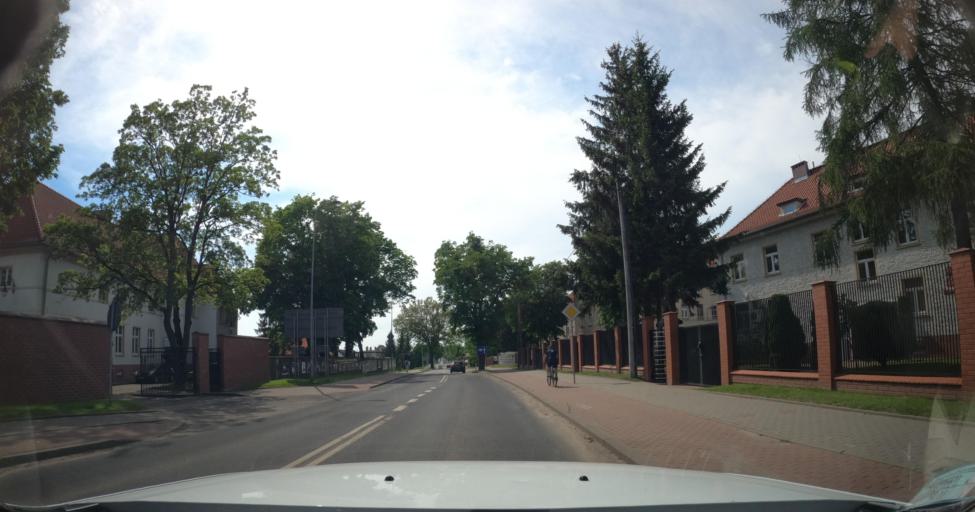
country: PL
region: Warmian-Masurian Voivodeship
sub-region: Powiat lidzbarski
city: Lidzbark Warminski
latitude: 54.1271
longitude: 20.5658
